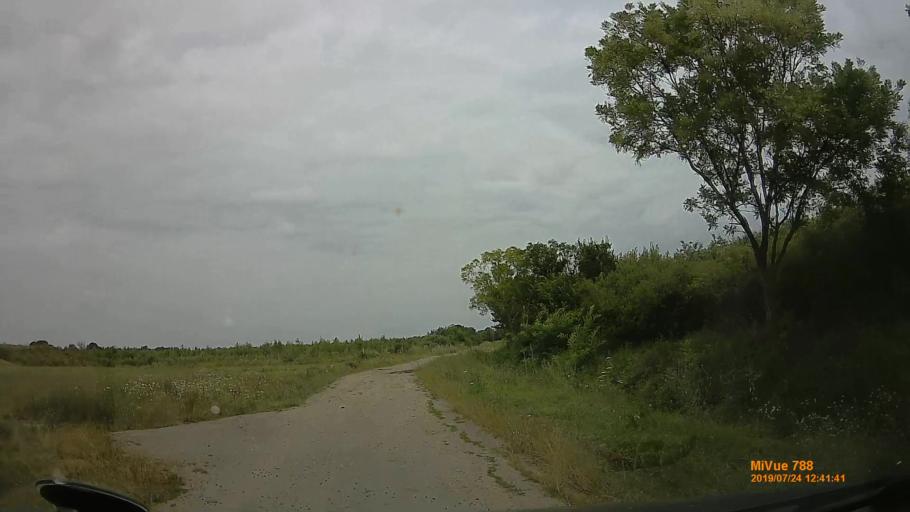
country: HU
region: Szabolcs-Szatmar-Bereg
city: Aranyosapati
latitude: 48.1969
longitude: 22.3207
